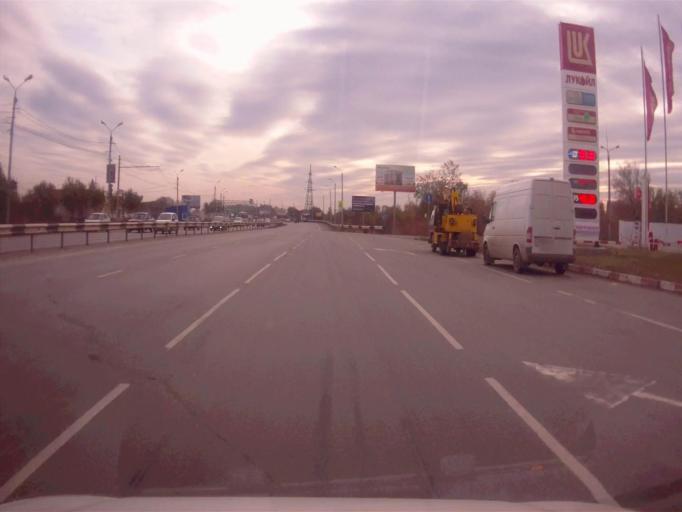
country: RU
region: Chelyabinsk
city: Novosineglazovskiy
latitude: 55.0757
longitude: 61.3883
